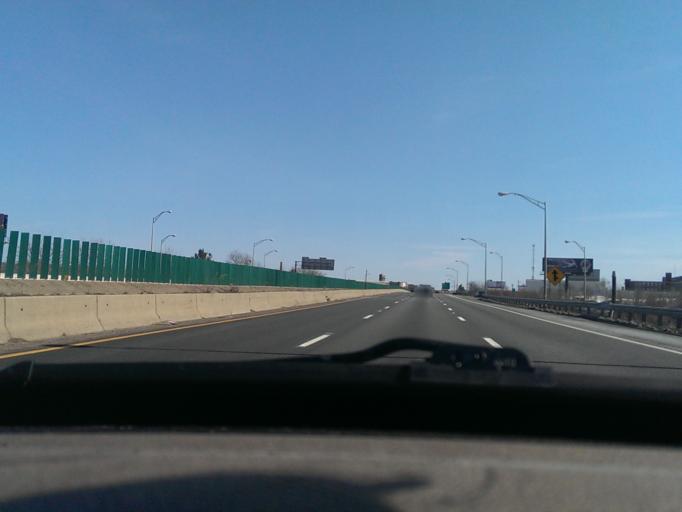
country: US
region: Massachusetts
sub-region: Bristol County
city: Fall River
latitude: 41.6964
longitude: -71.1499
